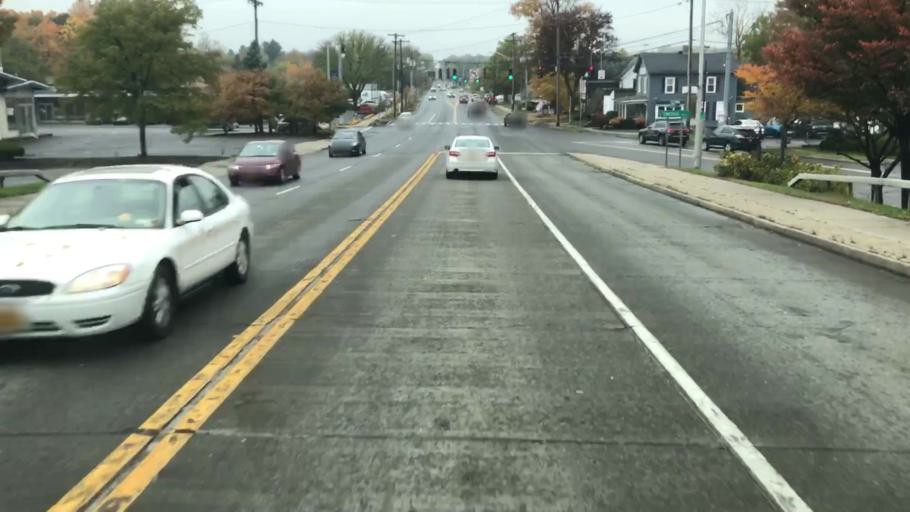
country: US
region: New York
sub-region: Onondaga County
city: Fayetteville
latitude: 43.0293
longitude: -76.0137
